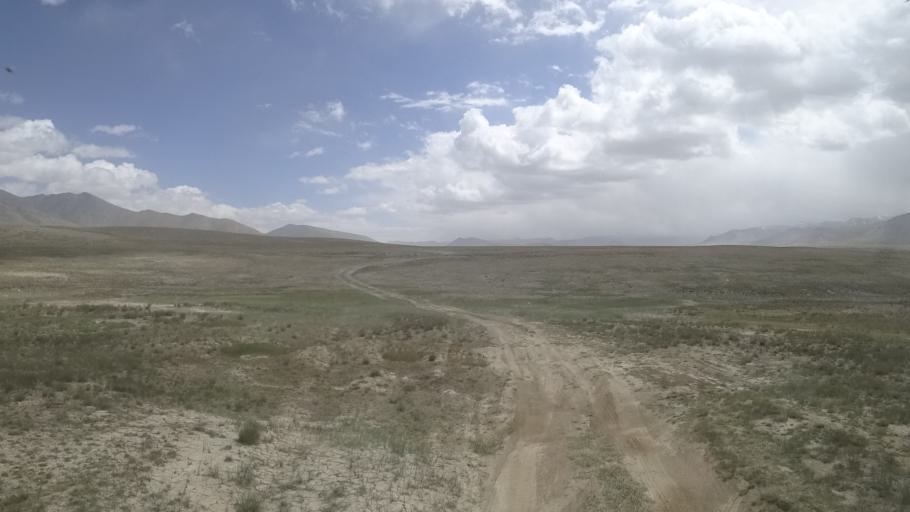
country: TJ
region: Gorno-Badakhshan
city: Murghob
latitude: 37.4728
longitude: 73.9674
